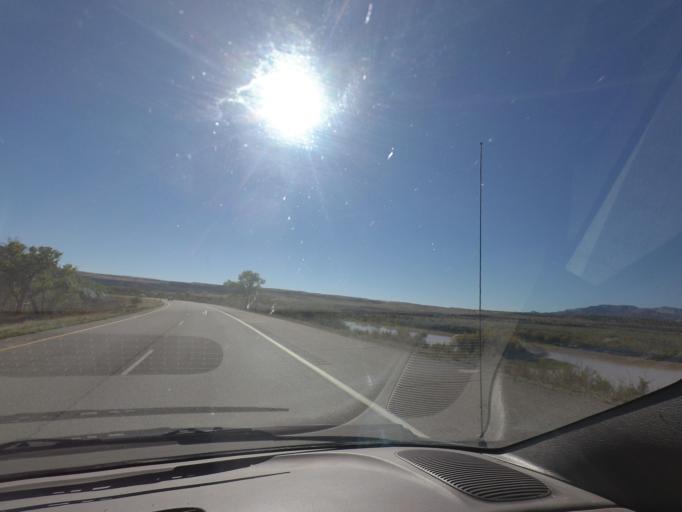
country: US
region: Colorado
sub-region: Mesa County
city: Palisade
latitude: 39.2787
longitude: -108.2465
